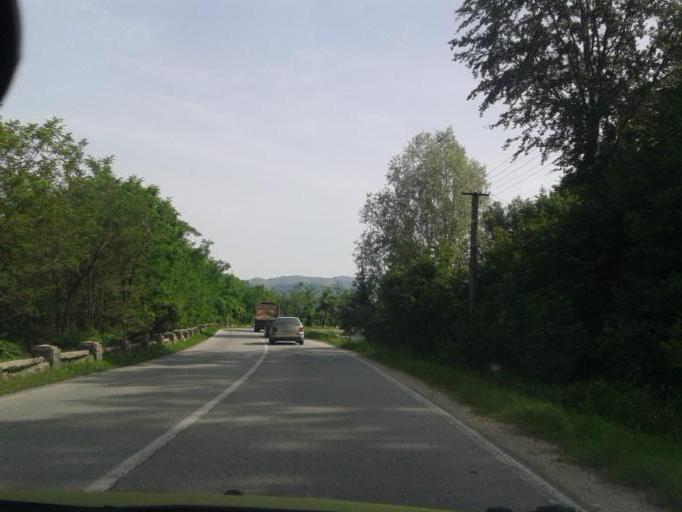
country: RO
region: Valcea
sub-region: Comuna Costesti
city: Costesti
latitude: 45.1374
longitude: 24.0662
